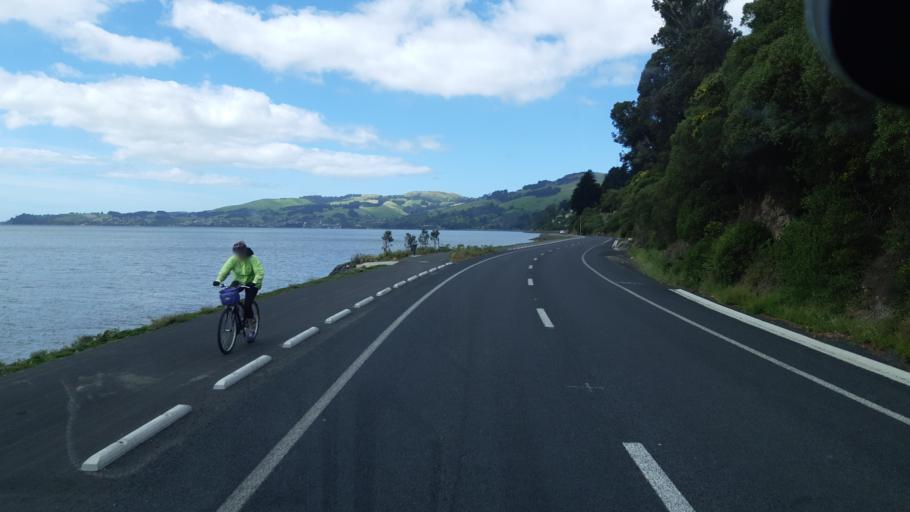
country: NZ
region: Otago
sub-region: Dunedin City
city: Dunedin
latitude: -45.8789
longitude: 170.5377
